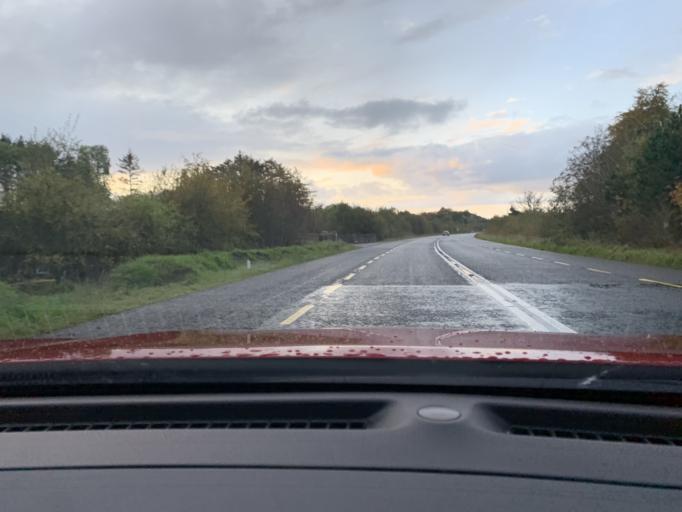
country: IE
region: Connaught
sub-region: County Leitrim
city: Carrick-on-Shannon
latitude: 53.9497
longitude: -8.1476
